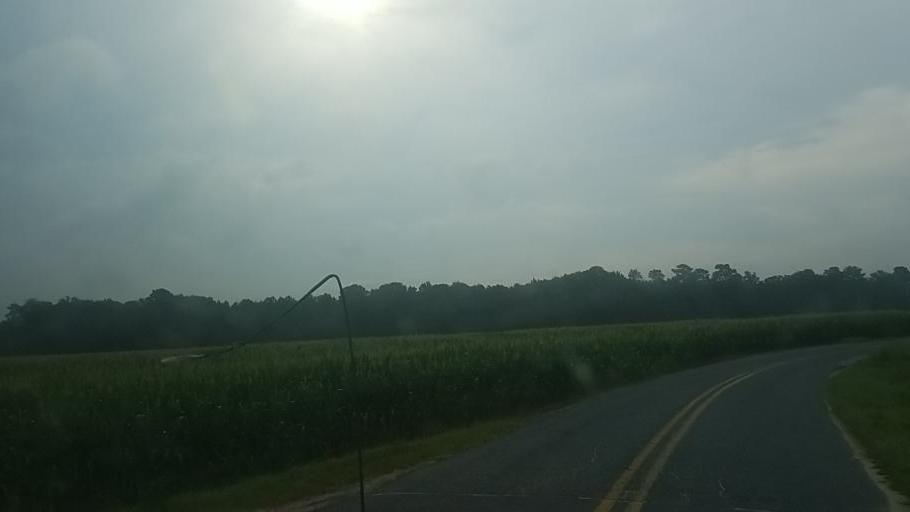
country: US
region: Maryland
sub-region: Wicomico County
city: Pittsville
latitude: 38.4387
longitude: -75.3288
